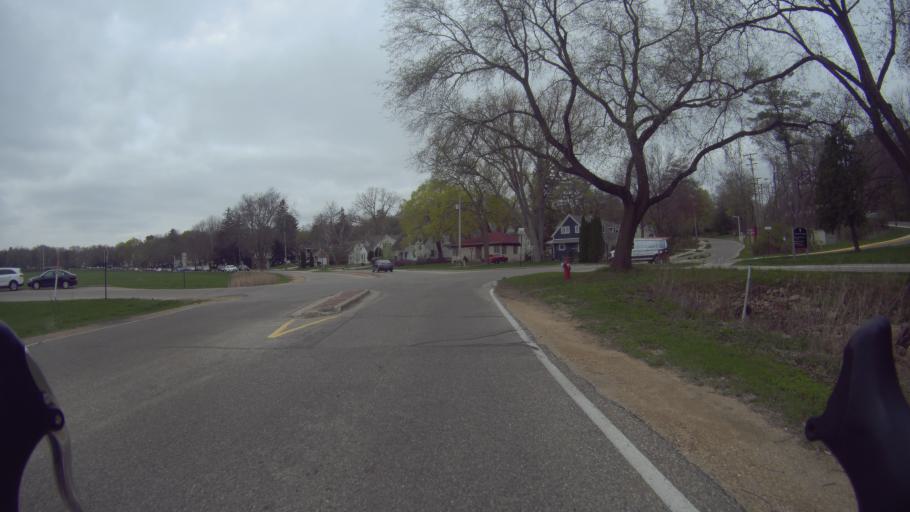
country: US
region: Wisconsin
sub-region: Dane County
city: Shorewood Hills
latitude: 43.0826
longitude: -89.4365
